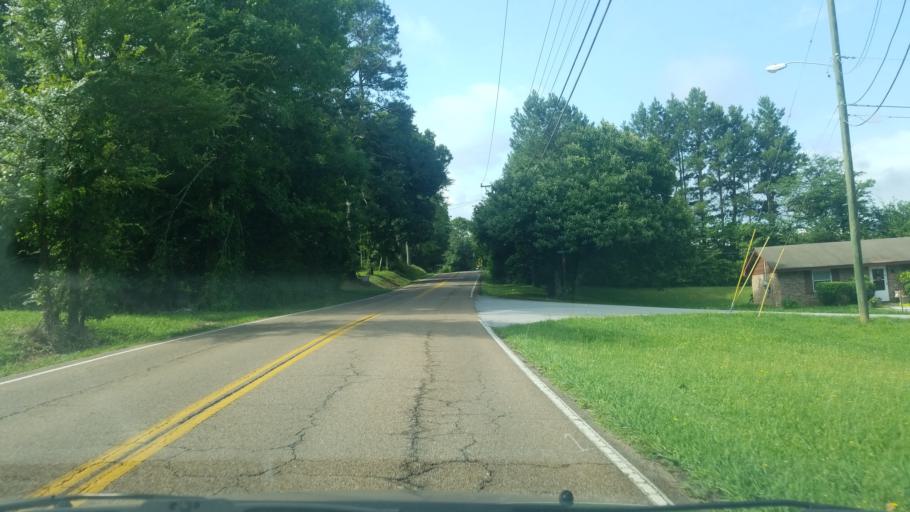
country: US
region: Tennessee
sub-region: Hamilton County
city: Apison
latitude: 35.0334
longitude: -85.0252
